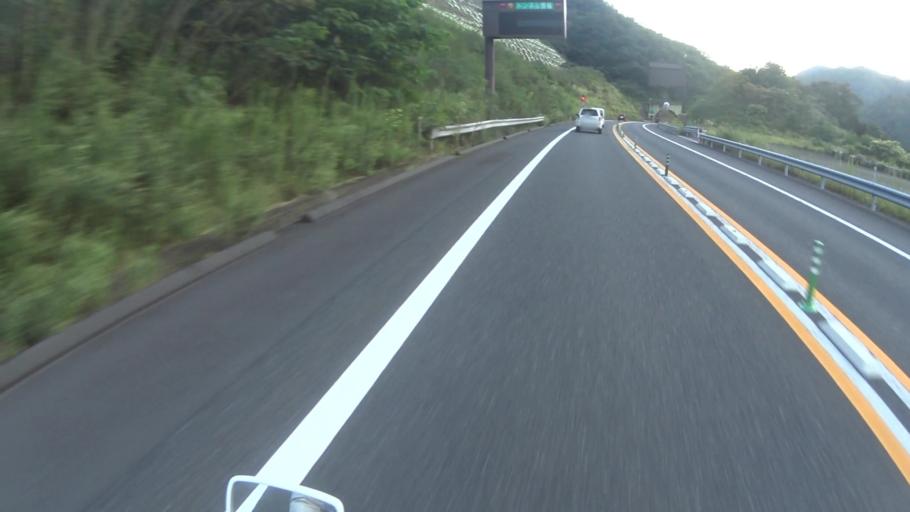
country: JP
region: Kyoto
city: Miyazu
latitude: 35.4718
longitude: 135.1757
